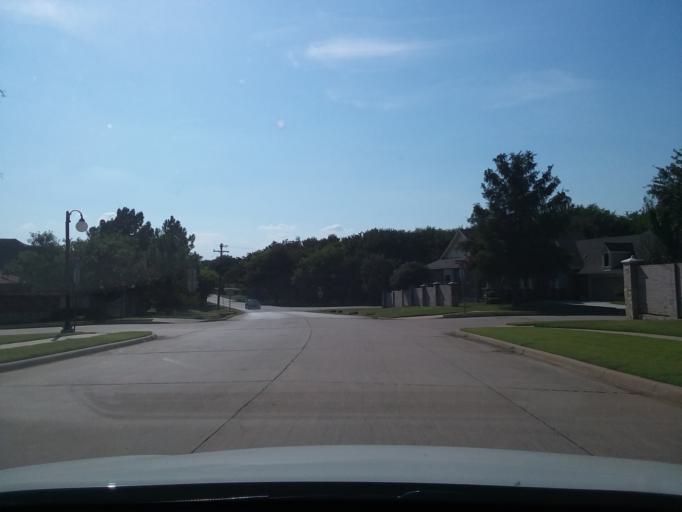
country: US
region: Texas
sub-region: Denton County
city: Double Oak
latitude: 33.0583
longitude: -97.0960
